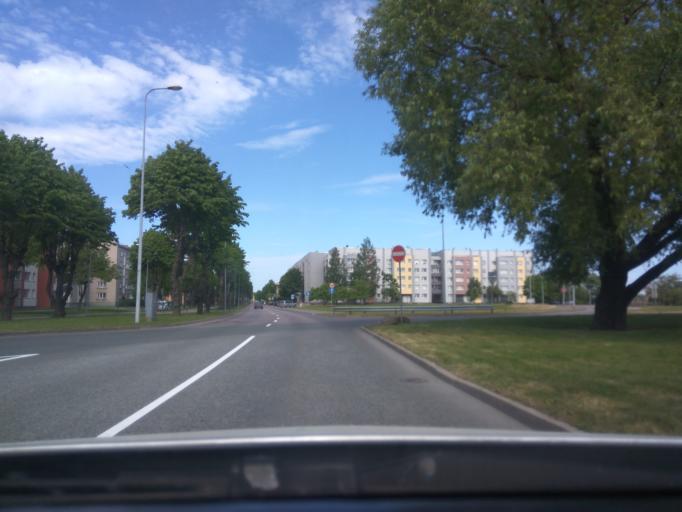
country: LV
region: Ventspils
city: Ventspils
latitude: 57.3903
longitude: 21.5821
